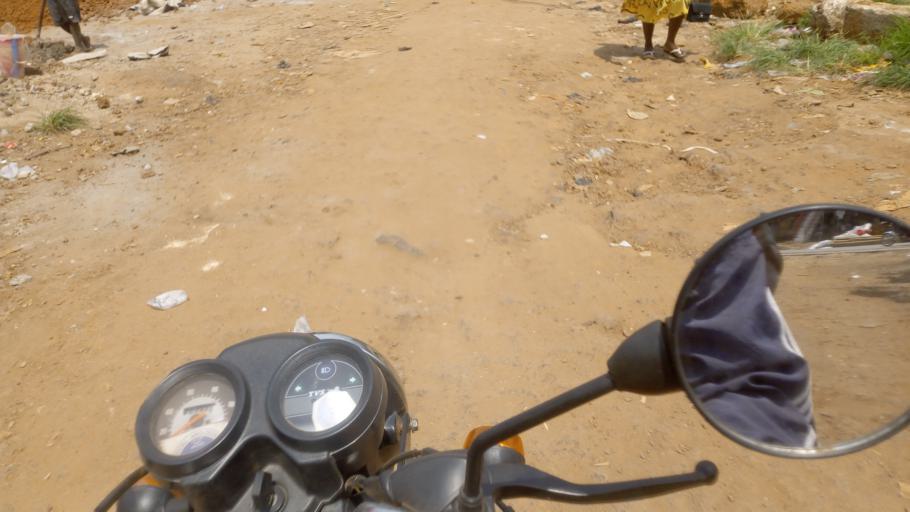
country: SL
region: Western Area
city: Waterloo
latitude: 8.3260
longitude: -13.0722
